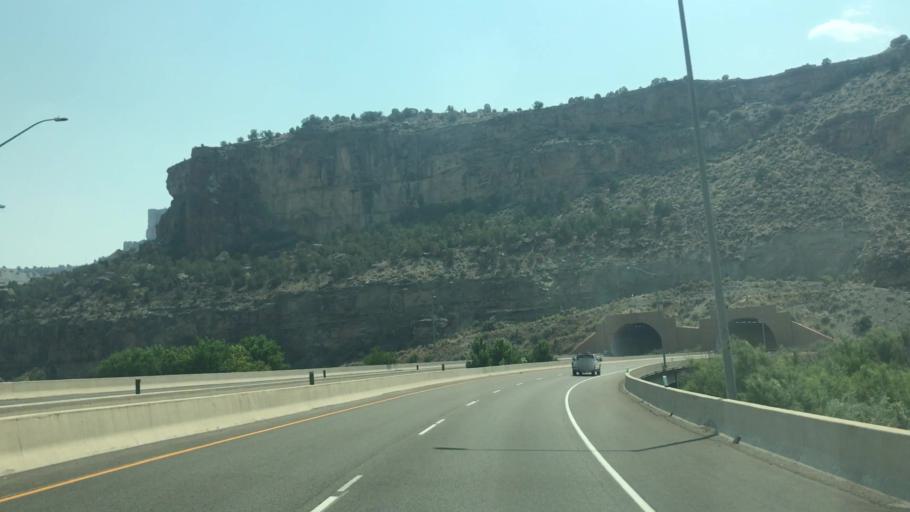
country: US
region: Colorado
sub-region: Mesa County
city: Palisade
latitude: 39.1982
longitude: -108.2681
